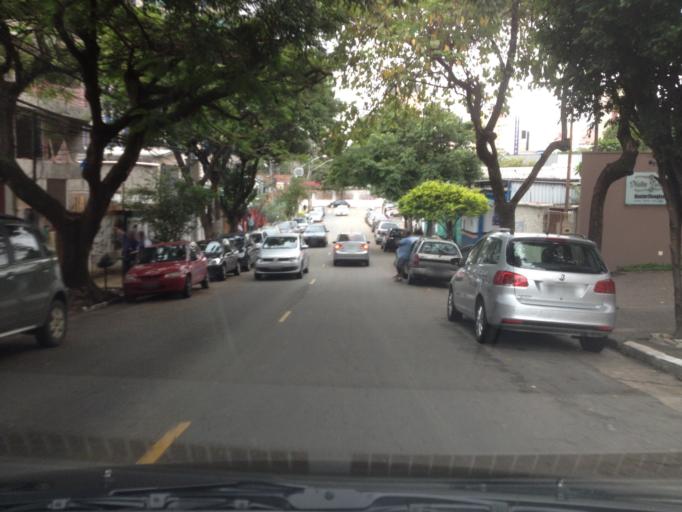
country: BR
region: Sao Paulo
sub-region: Sao Paulo
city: Sao Paulo
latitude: -23.5574
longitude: -46.6878
